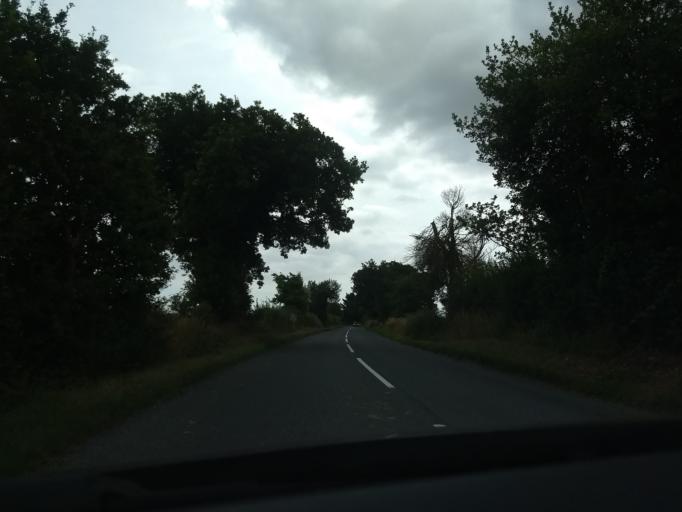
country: GB
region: England
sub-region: Suffolk
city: Ipswich
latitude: 51.9934
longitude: 1.1937
